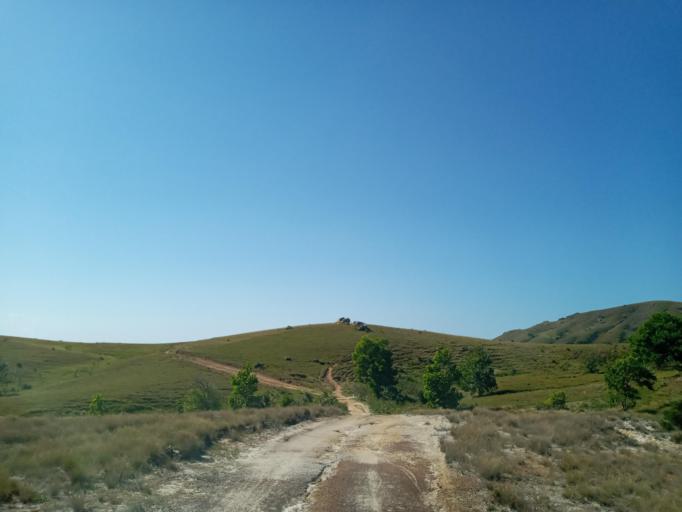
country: MG
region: Anosy
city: Fort Dauphin
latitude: -24.9107
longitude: 47.0722
